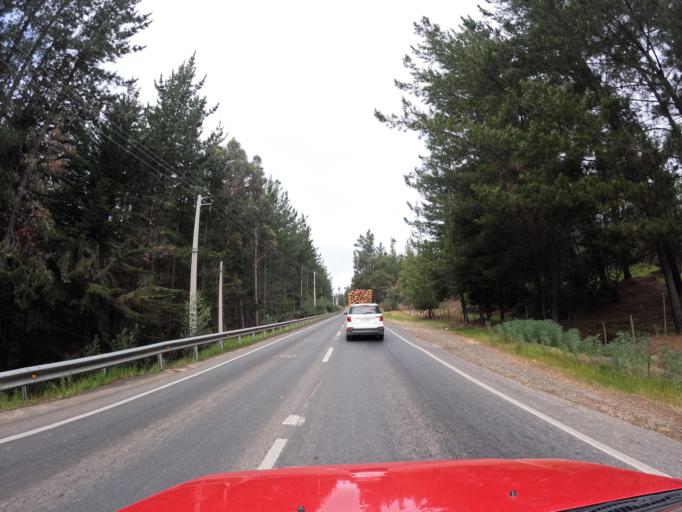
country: CL
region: O'Higgins
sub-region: Provincia de Colchagua
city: Santa Cruz
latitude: -34.3588
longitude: -71.8922
